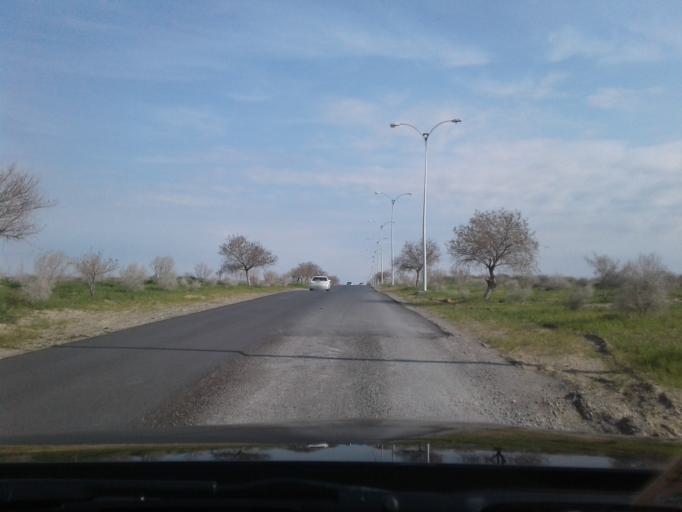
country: TM
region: Ahal
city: Ashgabat
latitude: 38.0919
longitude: 58.3827
